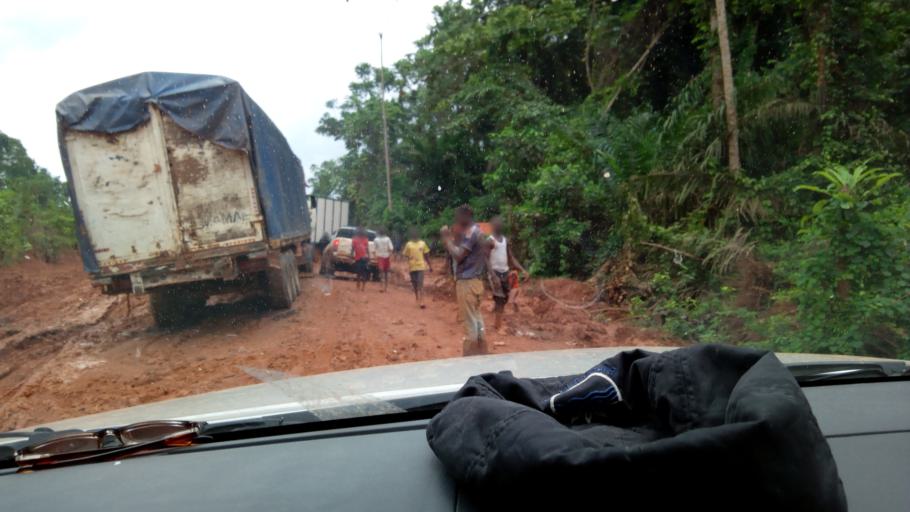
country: LR
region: Grand Gedeh
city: Zwedru
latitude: 6.1908
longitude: -8.3231
